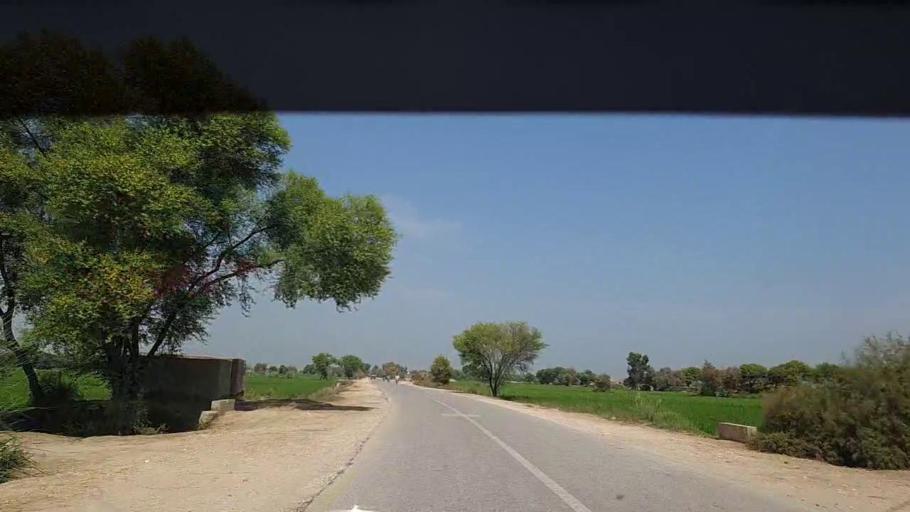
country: PK
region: Sindh
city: Thul
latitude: 28.1428
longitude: 68.8178
